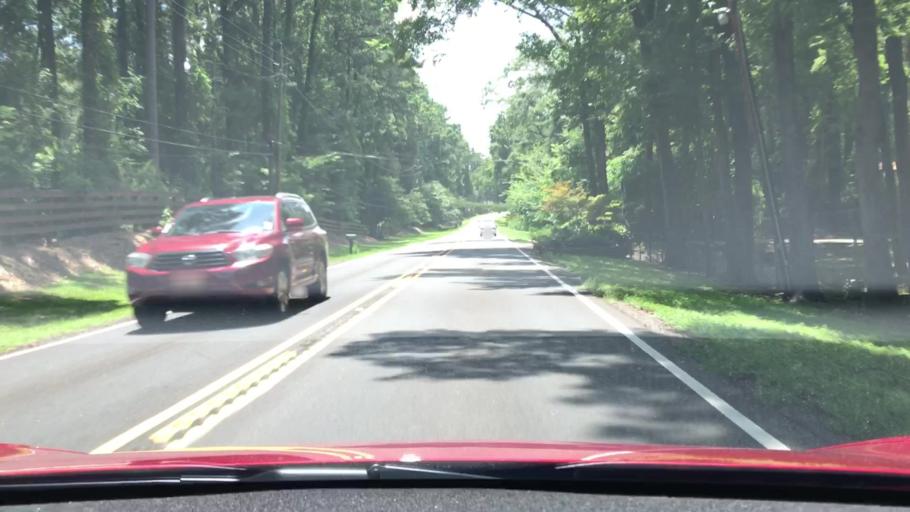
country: US
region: Louisiana
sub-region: Bossier Parish
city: Bossier City
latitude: 32.3673
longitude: -93.6859
